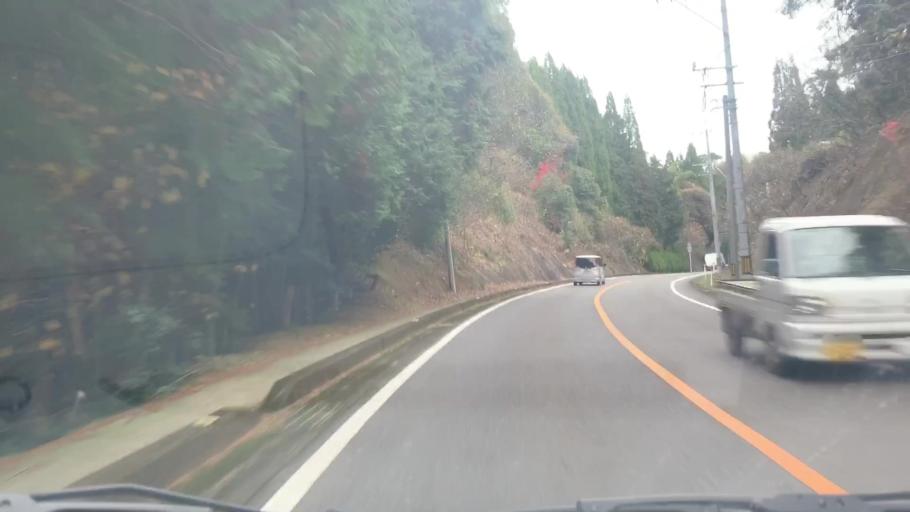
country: JP
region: Saga Prefecture
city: Ureshinomachi-shimojuku
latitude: 33.1619
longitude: 129.9678
